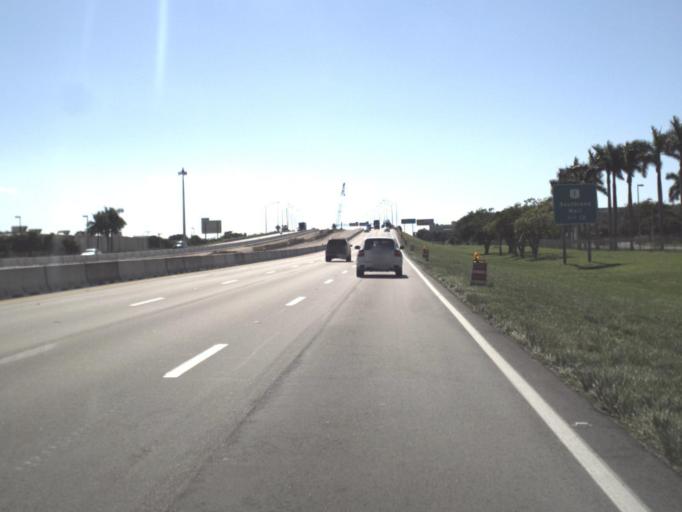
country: US
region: Florida
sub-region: Miami-Dade County
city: South Miami Heights
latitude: 25.5879
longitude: -80.3684
